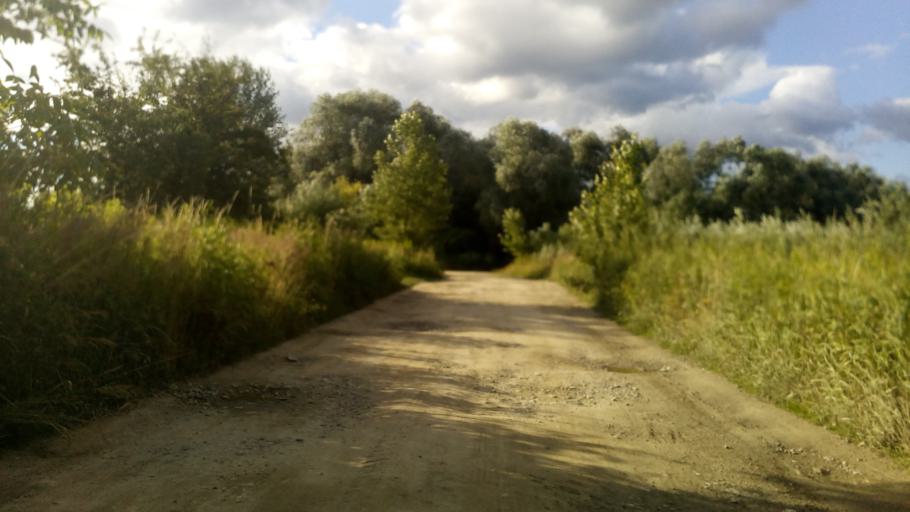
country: PL
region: Lesser Poland Voivodeship
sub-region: Powiat nowosadecki
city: Chelmiec
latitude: 49.6031
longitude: 20.6723
